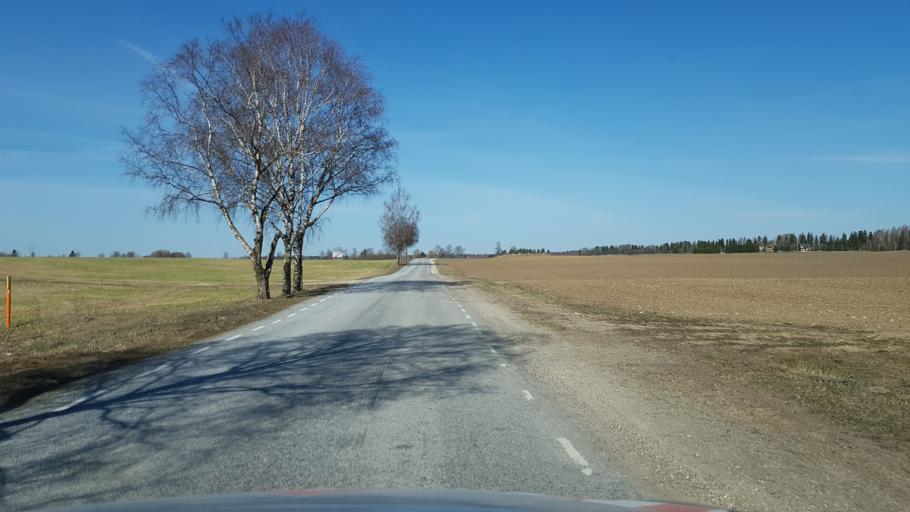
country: EE
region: Laeaene-Virumaa
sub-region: Vinni vald
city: Vinni
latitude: 59.2972
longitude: 26.4210
